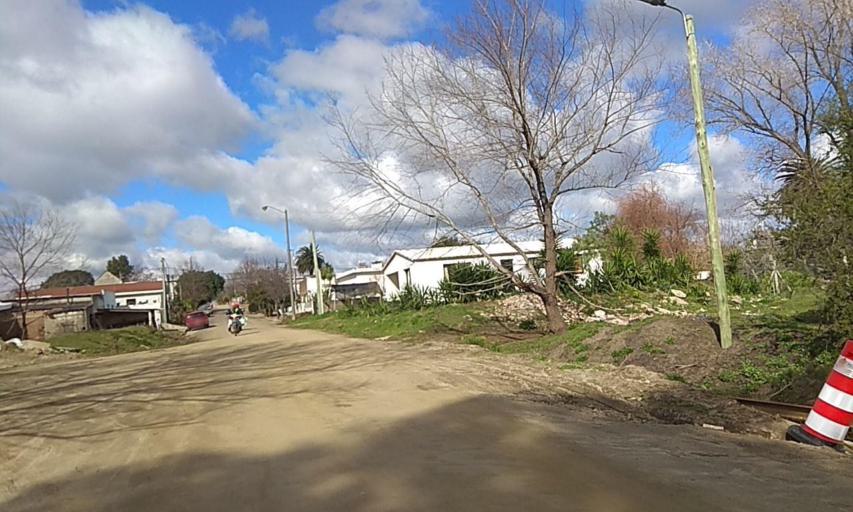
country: UY
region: Florida
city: Florida
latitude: -34.0901
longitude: -56.2226
